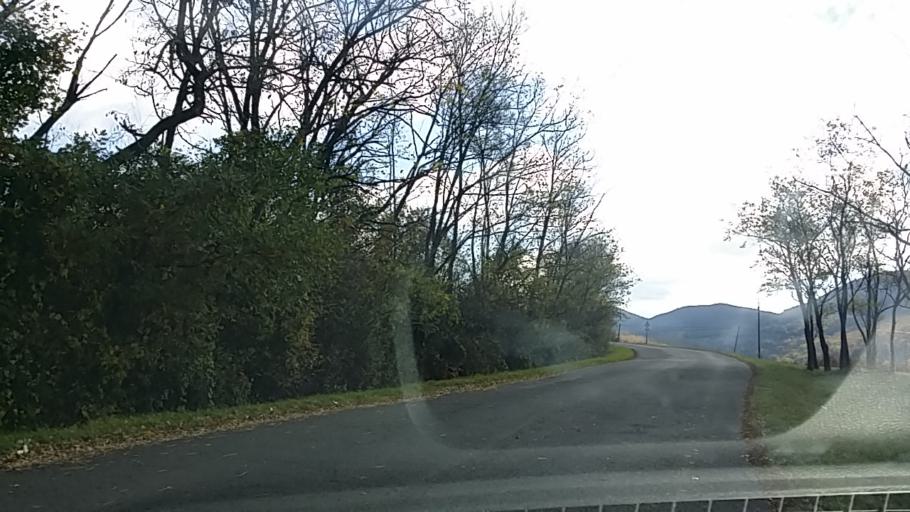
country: HU
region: Borsod-Abauj-Zemplen
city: Gonc
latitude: 48.3843
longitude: 21.3128
